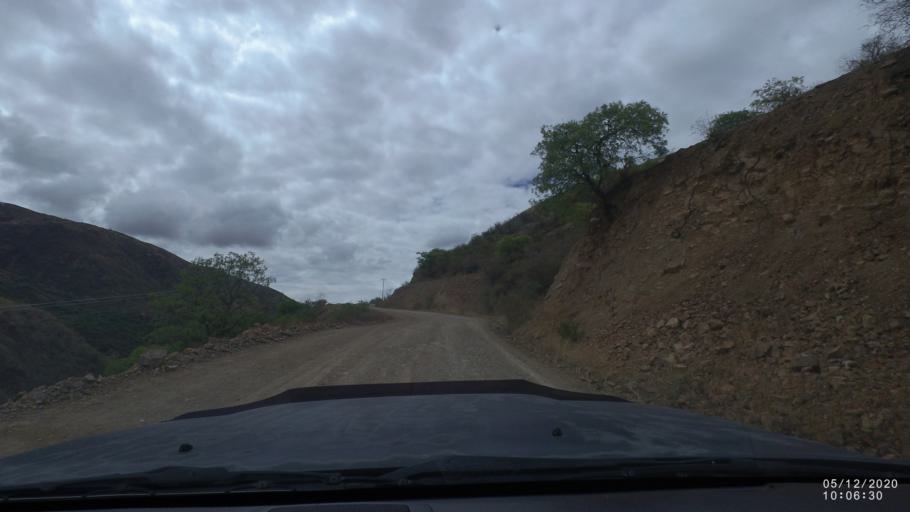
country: BO
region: Cochabamba
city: Sipe Sipe
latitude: -17.4762
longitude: -66.2846
